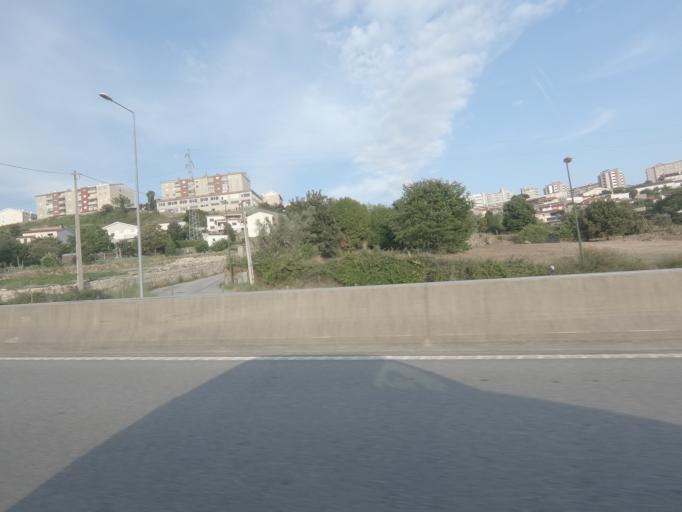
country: PT
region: Vila Real
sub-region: Vila Real
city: Vila Real
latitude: 41.3104
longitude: -7.7486
